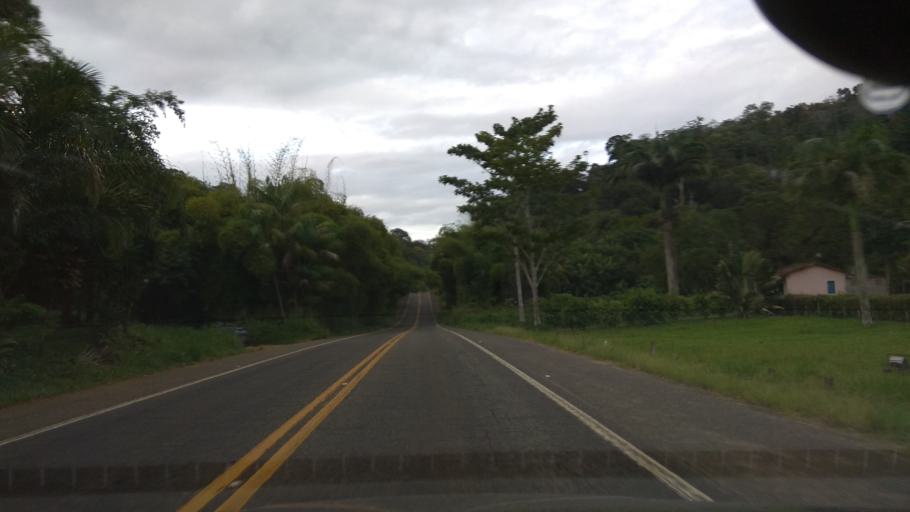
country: BR
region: Bahia
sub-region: Ubata
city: Ubata
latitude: -14.2302
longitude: -39.4354
